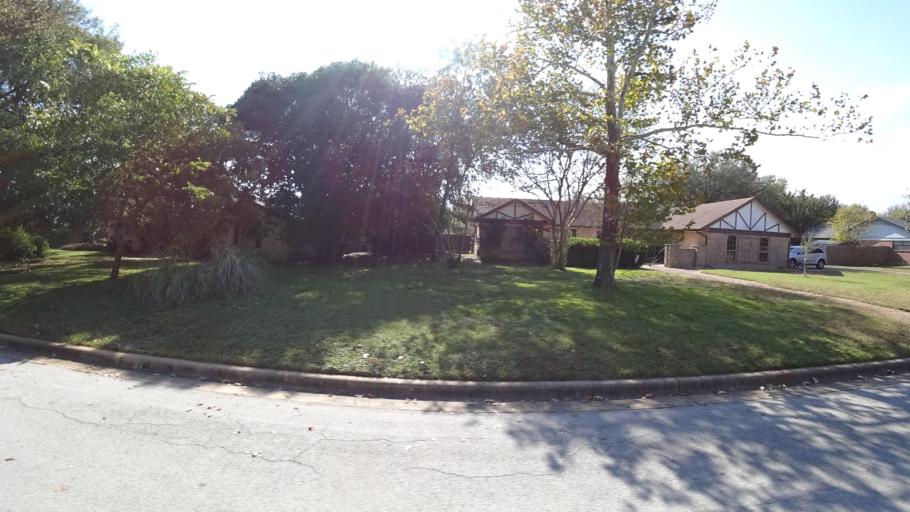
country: US
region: Texas
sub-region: Travis County
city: Shady Hollow
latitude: 30.1663
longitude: -97.8648
